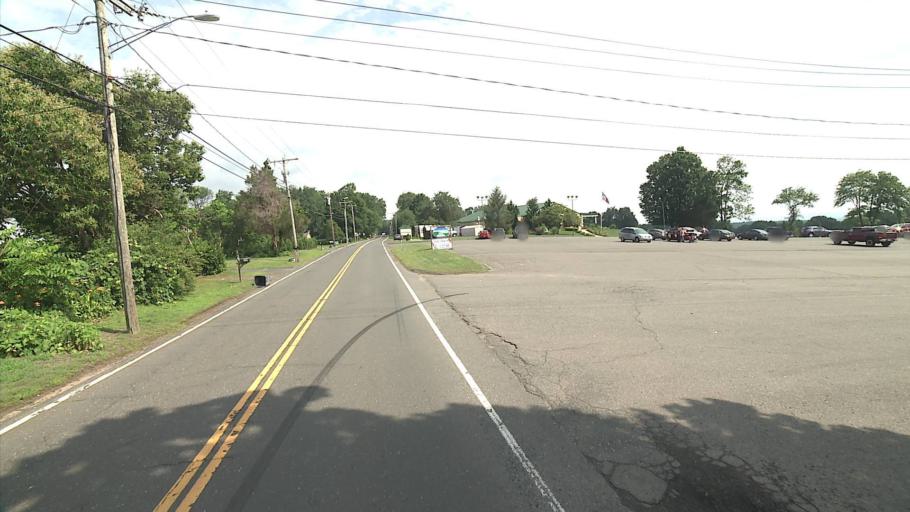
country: US
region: Connecticut
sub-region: New Haven County
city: Wolcott
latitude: 41.5682
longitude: -72.9479
